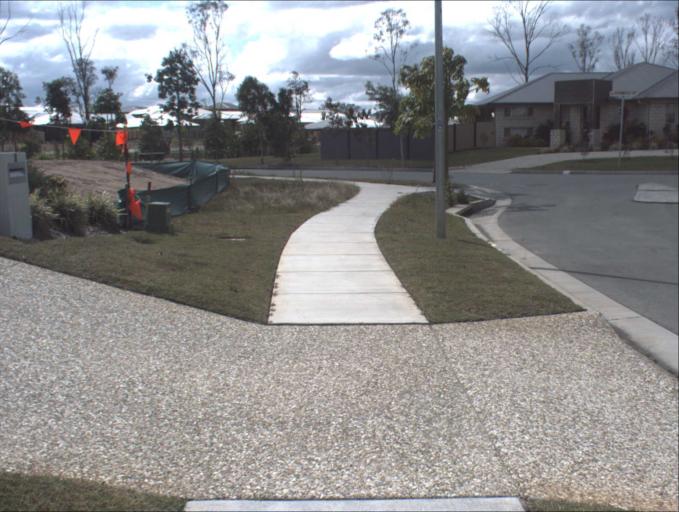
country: AU
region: Queensland
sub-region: Logan
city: Chambers Flat
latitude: -27.8009
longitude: 153.1062
